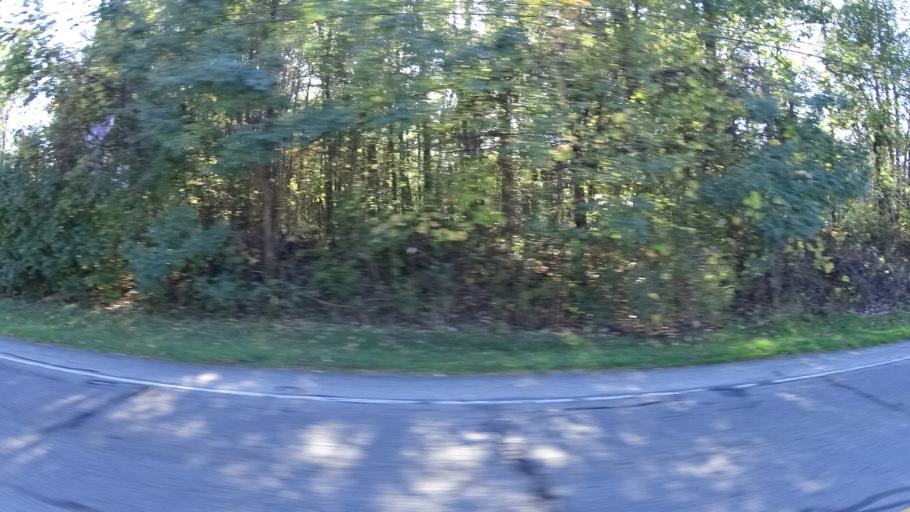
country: US
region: Ohio
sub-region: Lorain County
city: Lorain
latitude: 41.4272
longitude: -82.1493
